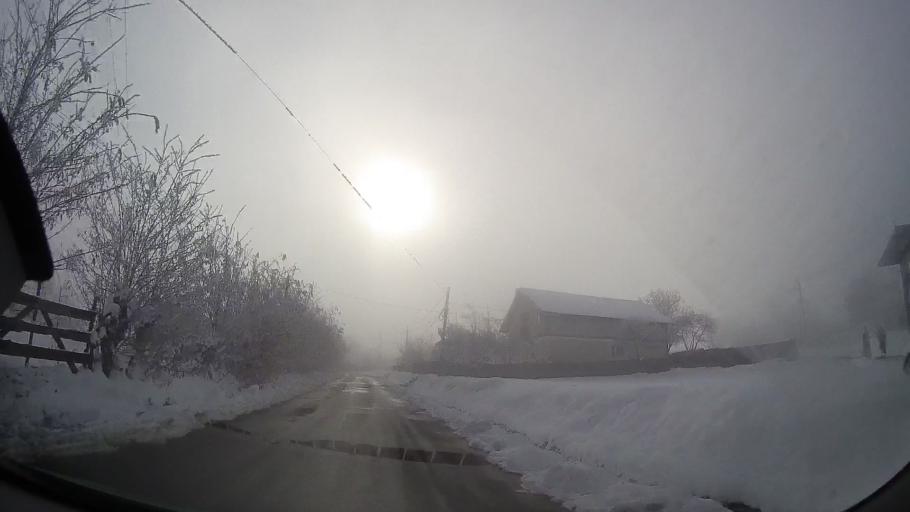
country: RO
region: Iasi
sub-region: Comuna Valea Seaca
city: Topile
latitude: 47.2563
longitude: 26.6661
